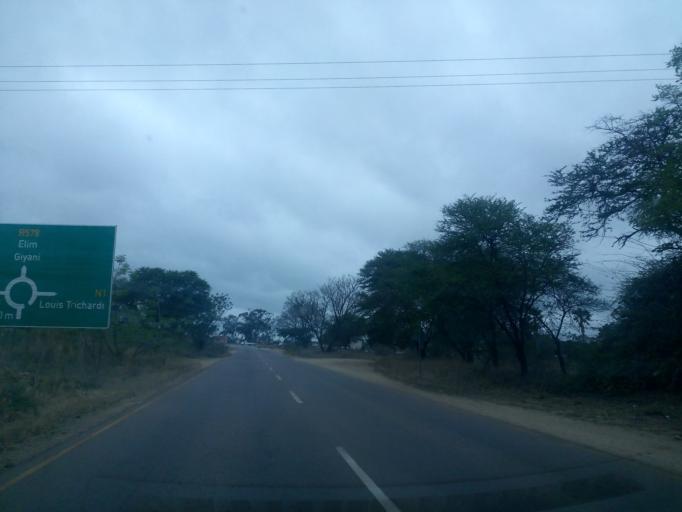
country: ZA
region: Limpopo
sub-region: Vhembe District Municipality
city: Louis Trichardt
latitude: -23.0786
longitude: 29.9060
